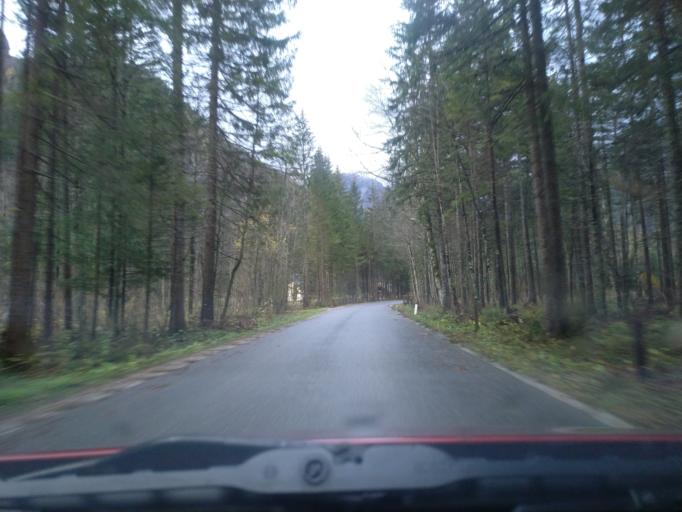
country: SI
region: Solcava
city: Solcava
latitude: 46.4062
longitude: 14.6358
